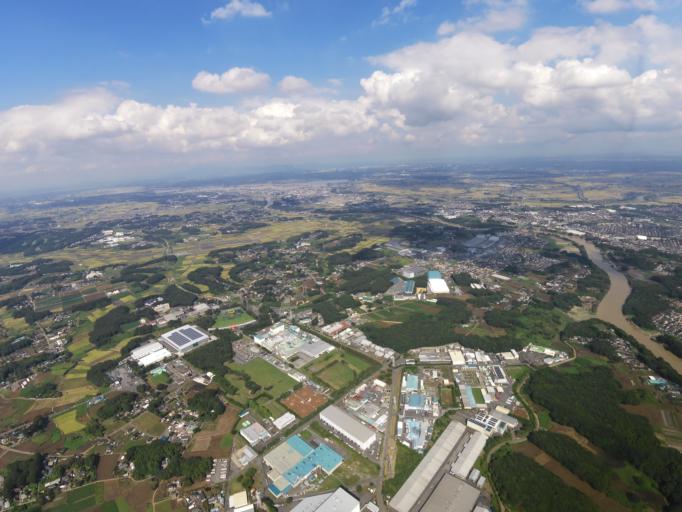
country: JP
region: Ibaraki
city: Mitsukaido
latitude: 35.9765
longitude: 139.9418
